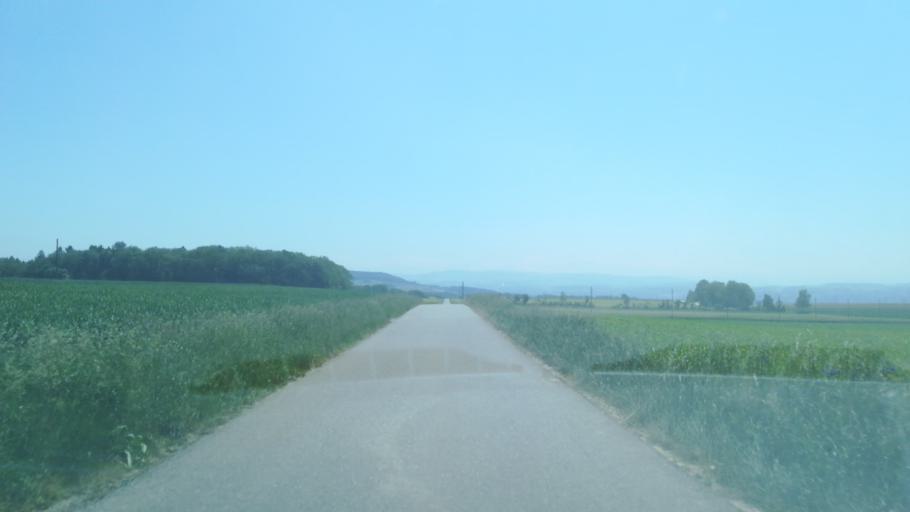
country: CH
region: Thurgau
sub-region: Kreuzlingen District
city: Ermatingen
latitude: 47.6328
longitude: 9.0771
